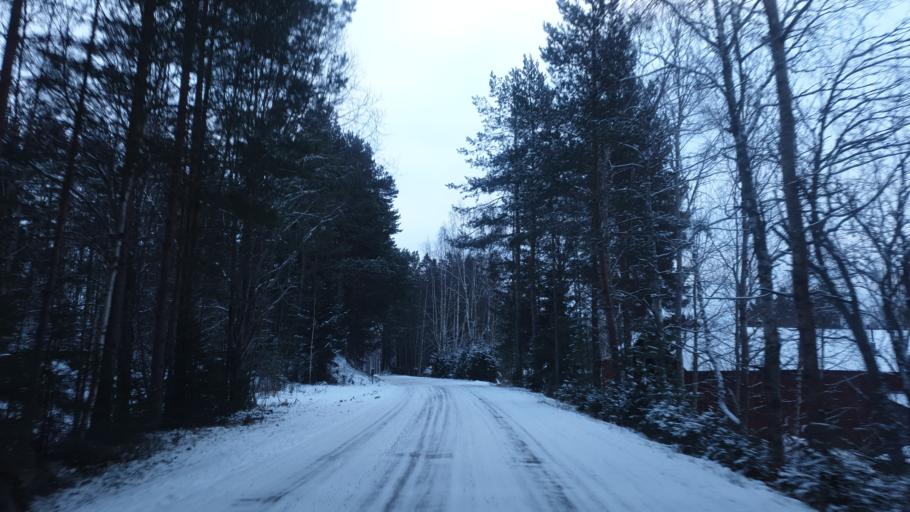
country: SE
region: Gaevleborg
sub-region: Bollnas Kommun
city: Kilafors
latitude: 61.2548
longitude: 16.5420
